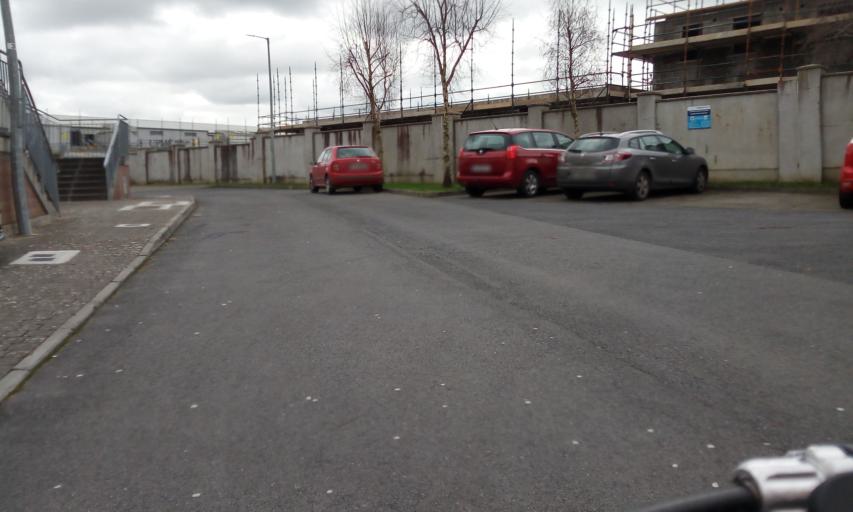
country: IE
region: Leinster
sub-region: Kilkenny
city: Kilkenny
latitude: 52.6580
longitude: -7.2412
